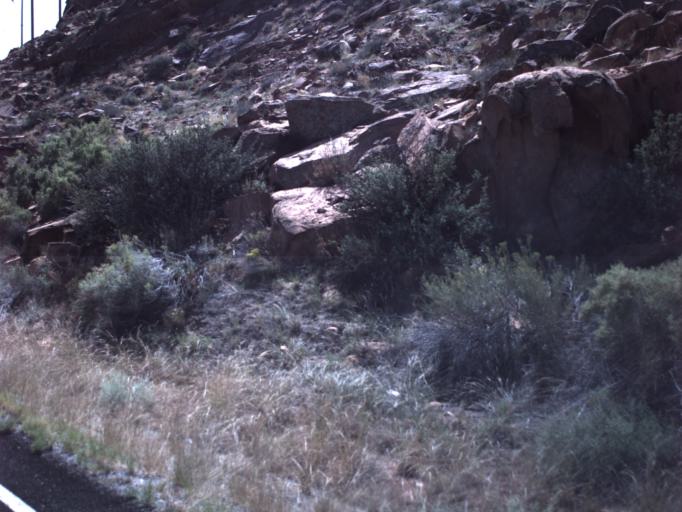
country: US
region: Utah
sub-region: Grand County
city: Moab
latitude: 38.5742
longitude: -109.5806
